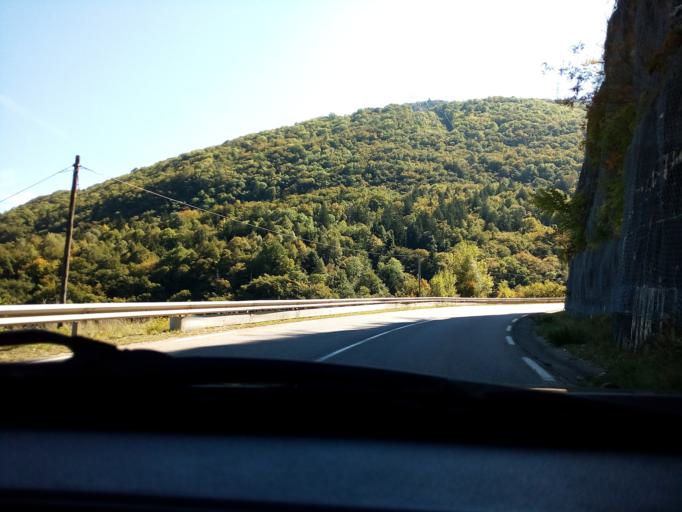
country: FR
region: Rhone-Alpes
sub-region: Departement de l'Isere
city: Sassenage
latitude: 45.2089
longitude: 5.6412
